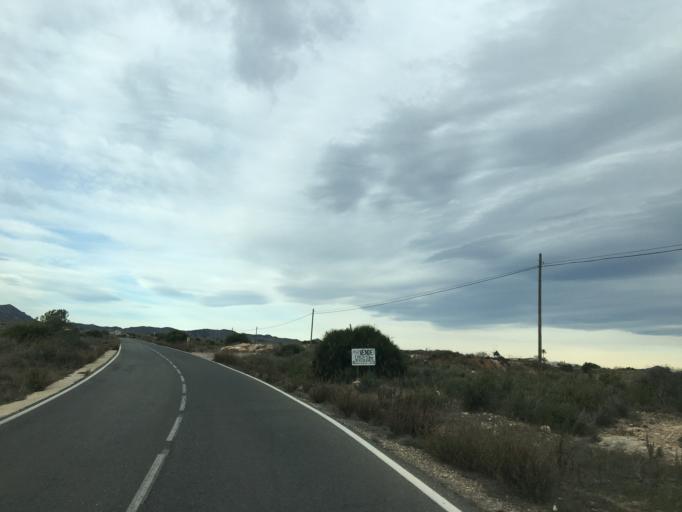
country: ES
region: Murcia
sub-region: Murcia
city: Fuente-Alamo de Murcia
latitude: 37.6193
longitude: -1.0738
